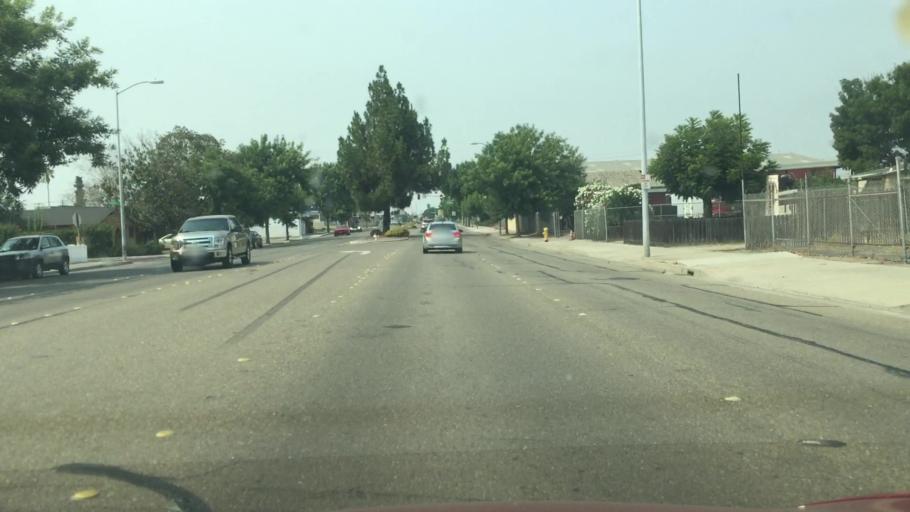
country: US
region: California
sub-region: San Joaquin County
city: Manteca
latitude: 37.7919
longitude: -121.2161
